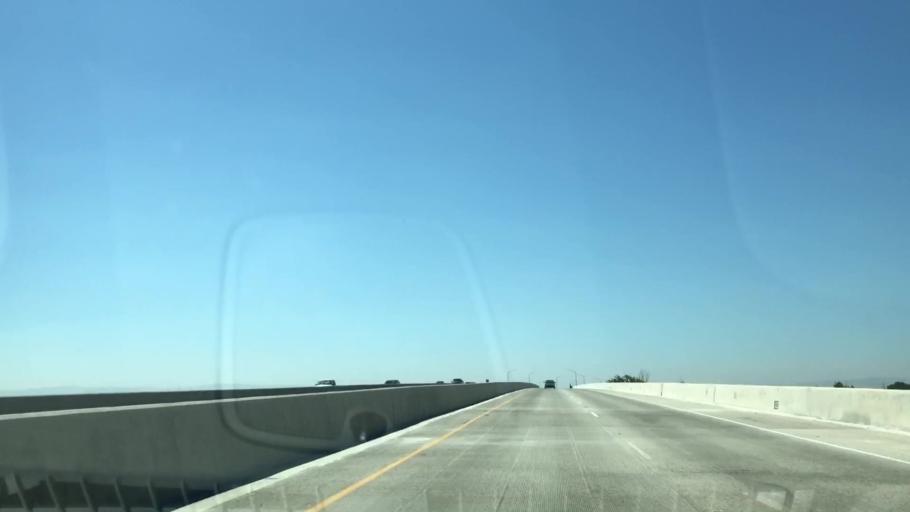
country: US
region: California
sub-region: San Joaquin County
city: Stockton
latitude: 37.9420
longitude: -121.3141
